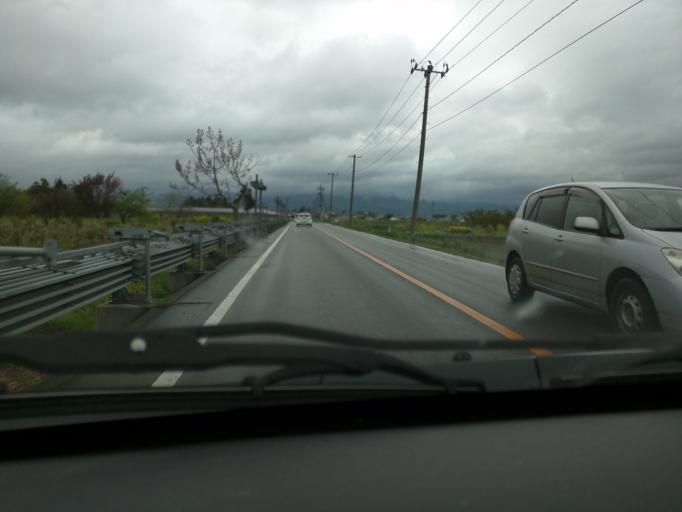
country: JP
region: Fukushima
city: Kitakata
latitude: 37.6207
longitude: 139.8649
